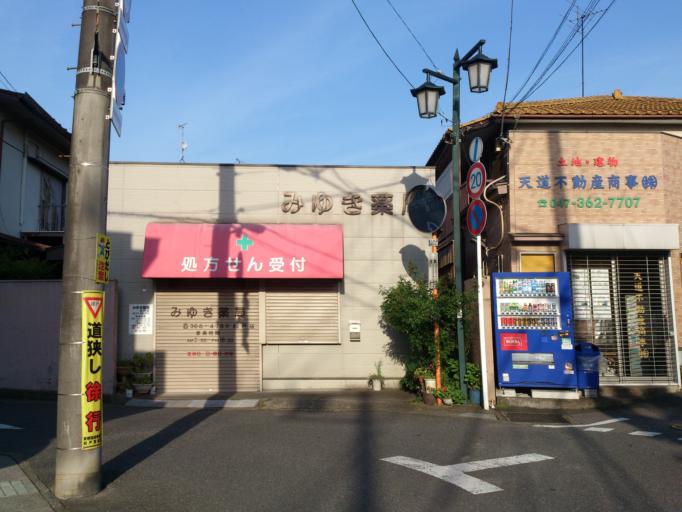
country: JP
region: Chiba
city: Matsudo
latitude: 35.7604
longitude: 139.9001
